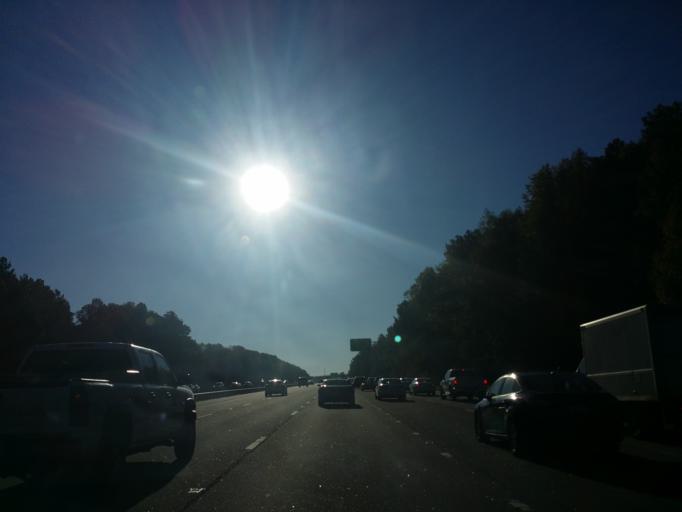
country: US
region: North Carolina
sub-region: Wake County
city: Cary
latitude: 35.8242
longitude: -78.7506
